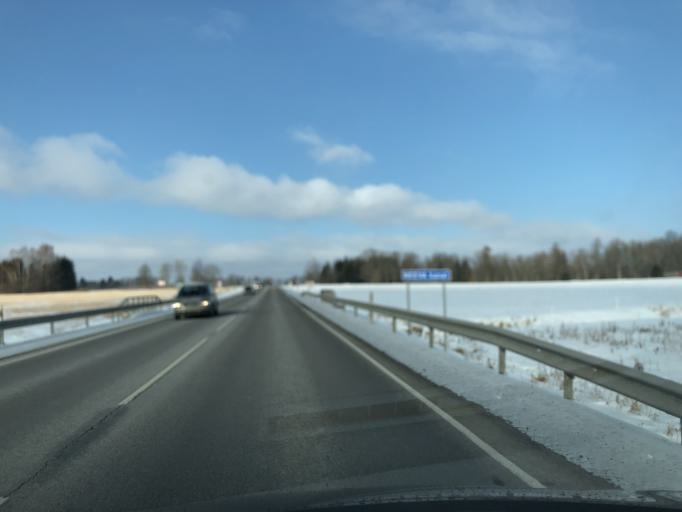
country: EE
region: Jaervamaa
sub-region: Paide linn
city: Paide
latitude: 58.8276
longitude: 25.7461
